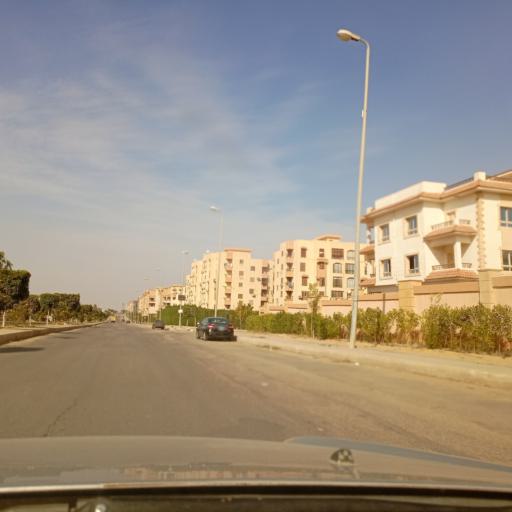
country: EG
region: Muhafazat al Qalyubiyah
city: Al Khankah
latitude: 30.0408
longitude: 31.4852
